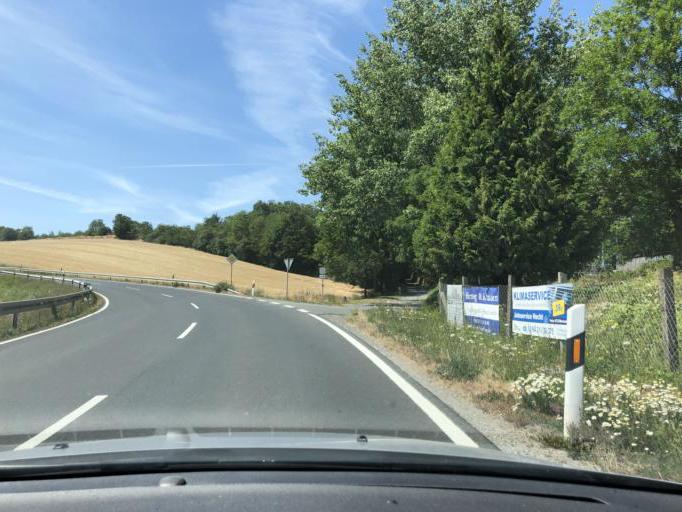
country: DE
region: Thuringia
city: Camburg
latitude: 51.0543
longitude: 11.6960
